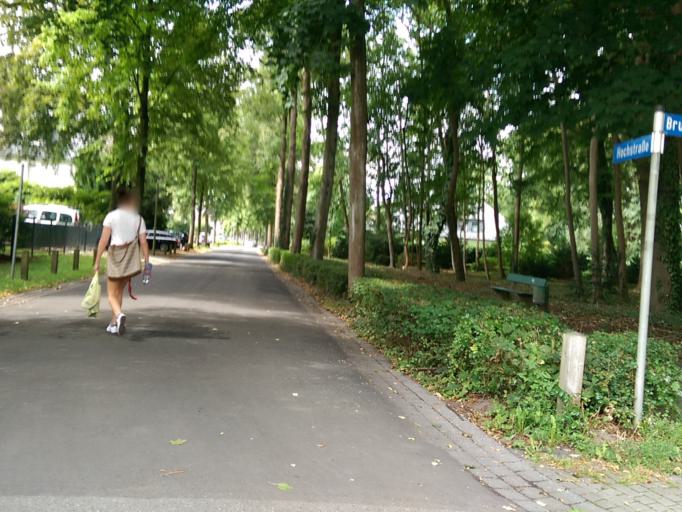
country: DE
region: North Rhine-Westphalia
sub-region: Regierungsbezirk Detmold
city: Guetersloh
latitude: 51.8983
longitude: 8.3873
